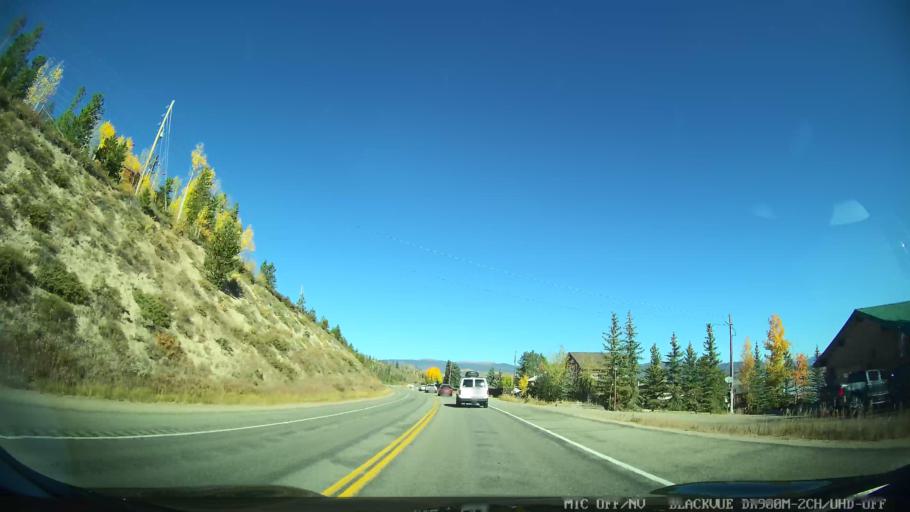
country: US
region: Colorado
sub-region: Grand County
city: Granby
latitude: 40.1578
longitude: -105.8907
